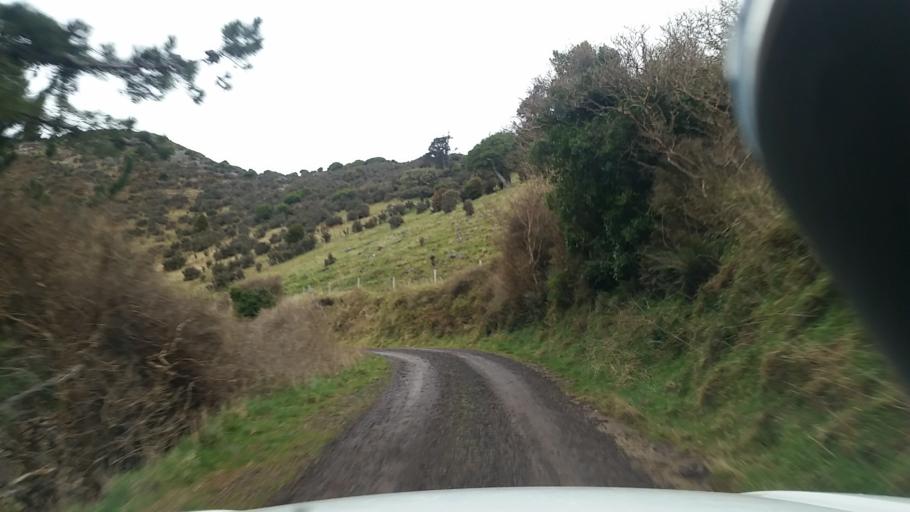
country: NZ
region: Canterbury
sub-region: Christchurch City
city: Christchurch
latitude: -43.7448
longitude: 173.0131
